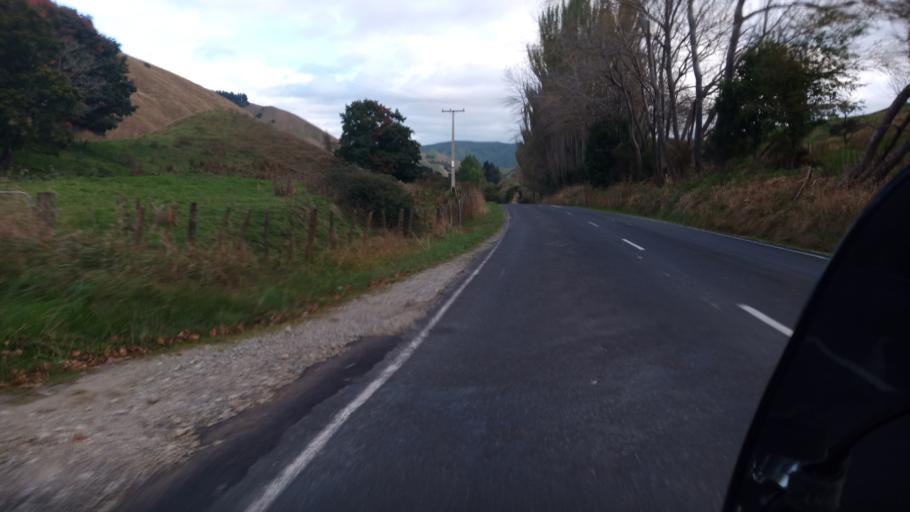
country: NZ
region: Gisborne
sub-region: Gisborne District
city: Gisborne
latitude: -38.5876
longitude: 177.7618
